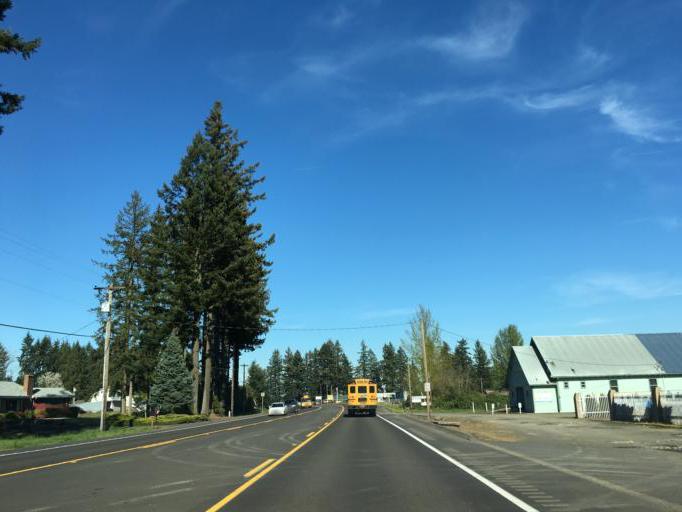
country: US
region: Oregon
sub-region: Clackamas County
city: Canby
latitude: 45.2376
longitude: -122.7402
